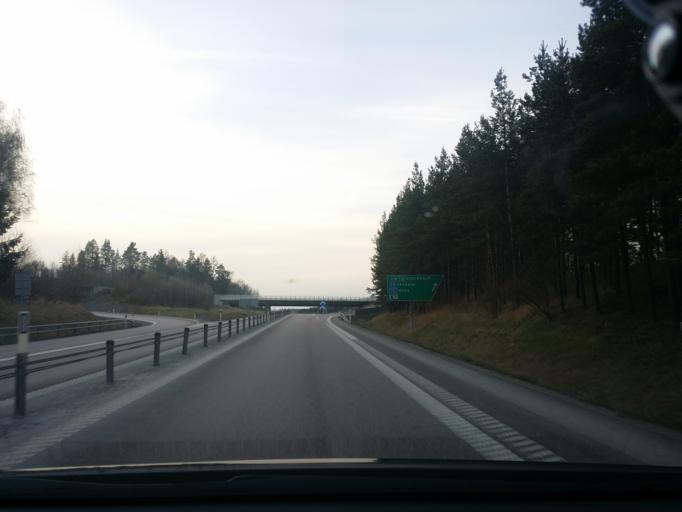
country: SE
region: Uppsala
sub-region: Enkopings Kommun
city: Enkoping
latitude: 59.6426
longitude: 17.0536
